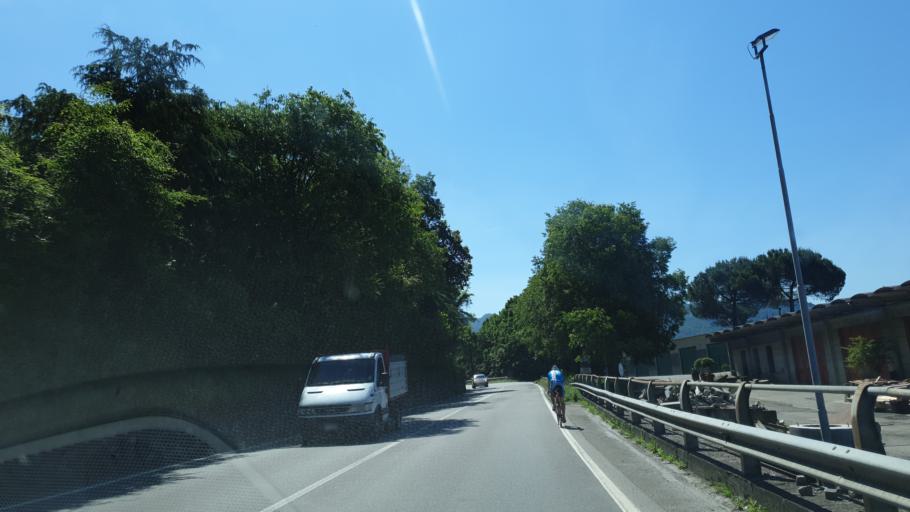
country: IT
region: Lombardy
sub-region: Provincia di Lecco
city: Monte Marenzo
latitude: 45.7561
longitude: 9.4560
